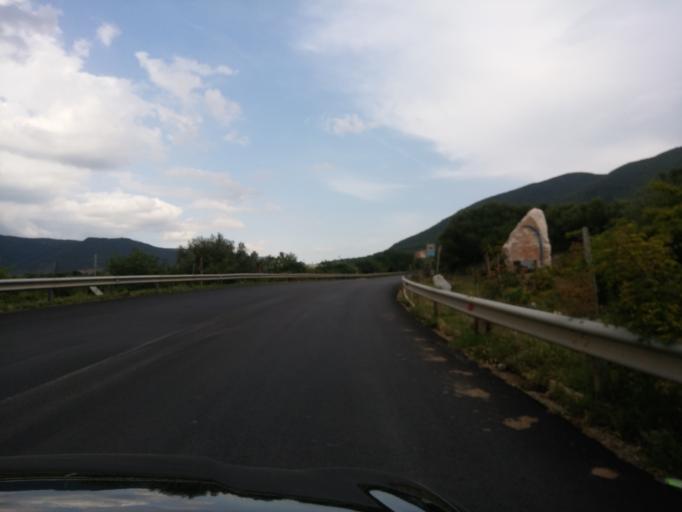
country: IT
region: Apulia
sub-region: Provincia di Foggia
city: Rignano Garganico
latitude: 41.7144
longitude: 15.5493
